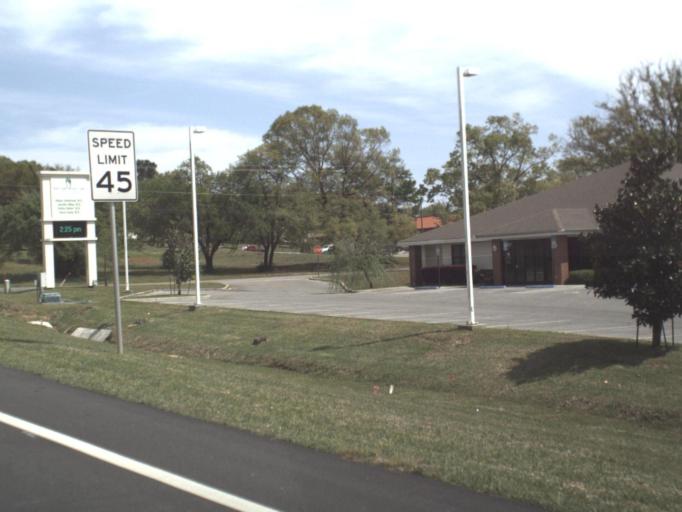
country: US
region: Florida
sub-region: Escambia County
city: Ferry Pass
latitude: 30.5320
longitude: -87.2193
